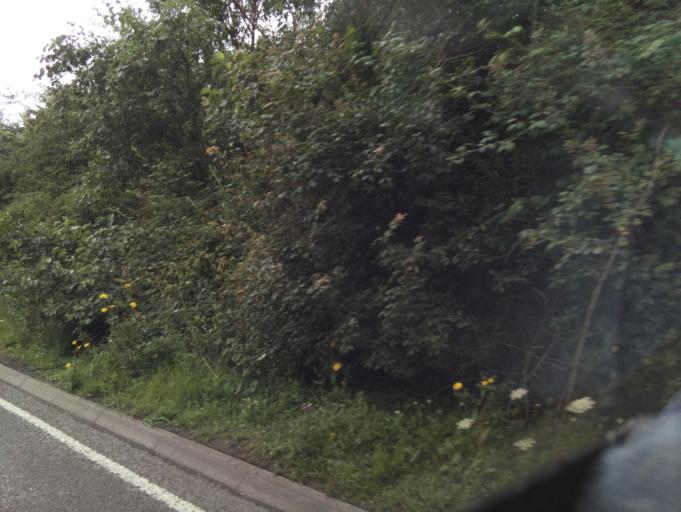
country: GB
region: England
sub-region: Northamptonshire
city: Geddington
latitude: 52.4454
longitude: -0.7352
